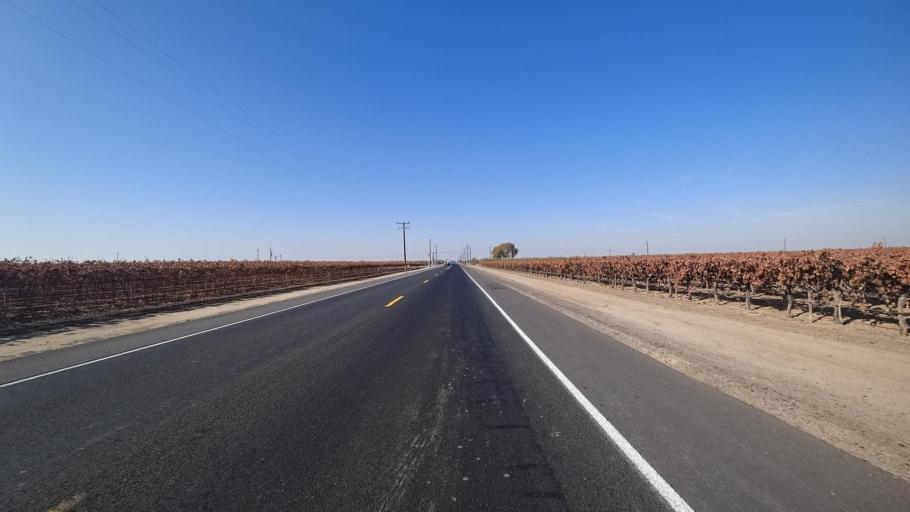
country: US
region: California
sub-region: Kern County
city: Delano
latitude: 35.7180
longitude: -119.2744
